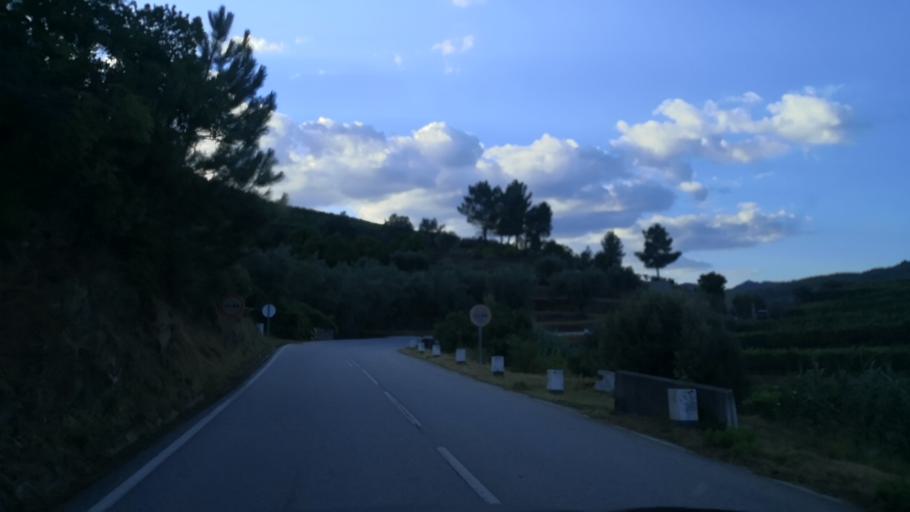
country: PT
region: Viseu
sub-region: Sao Joao da Pesqueira
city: Sao Joao da Pesqueira
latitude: 41.2371
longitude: -7.4310
